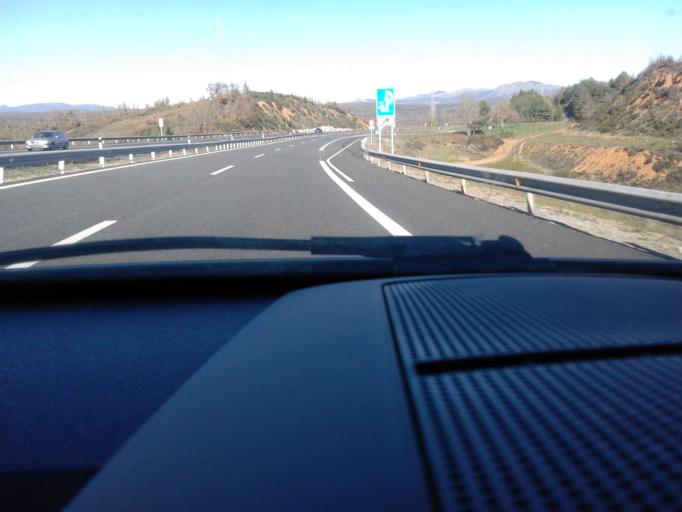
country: ES
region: Castille and Leon
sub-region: Provincia de Leon
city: Santa Maria de Ordas
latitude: 42.7099
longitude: -5.7954
